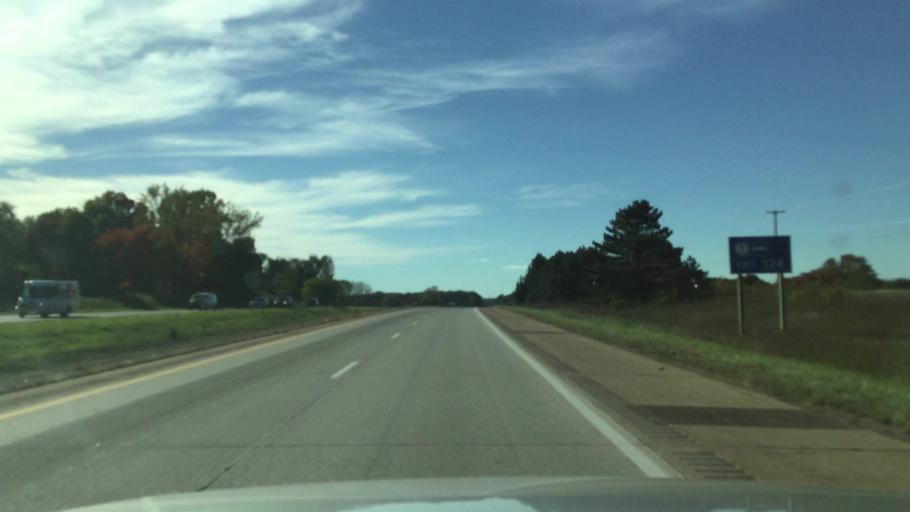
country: US
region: Michigan
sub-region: Calhoun County
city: Albion
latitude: 42.2623
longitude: -84.6996
